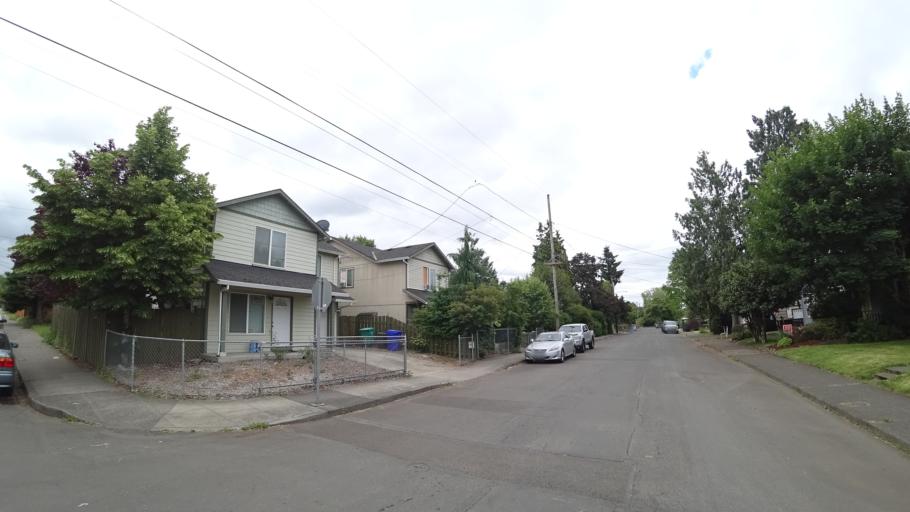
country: US
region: Oregon
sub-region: Multnomah County
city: Lents
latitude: 45.4869
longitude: -122.5768
